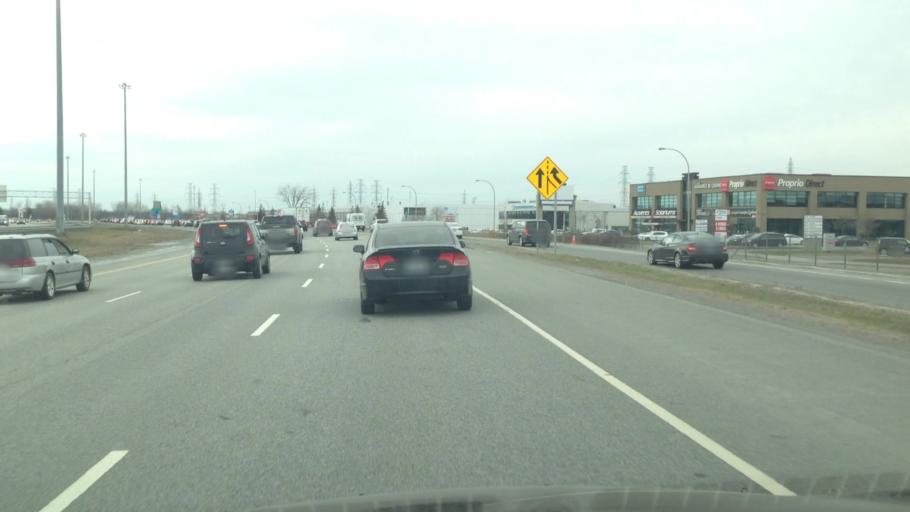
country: CA
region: Quebec
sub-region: Laurentides
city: Rosemere
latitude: 45.5814
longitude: -73.7605
